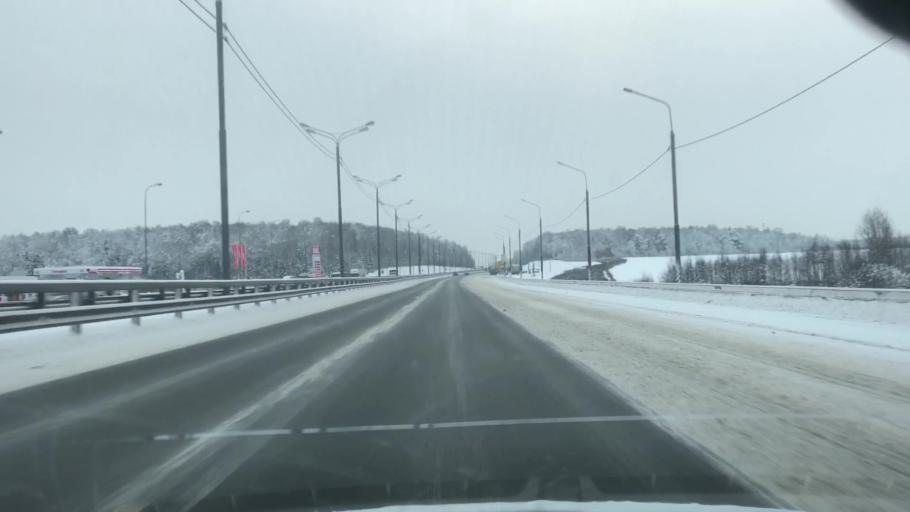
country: RU
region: Moskovskaya
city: Mikhnevo
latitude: 55.1837
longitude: 37.9026
